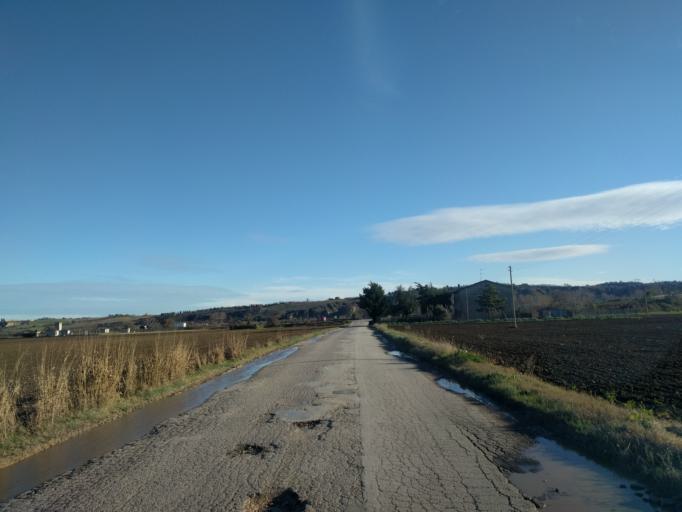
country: IT
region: The Marches
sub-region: Provincia di Pesaro e Urbino
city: Cuccurano
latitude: 43.7804
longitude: 12.9791
